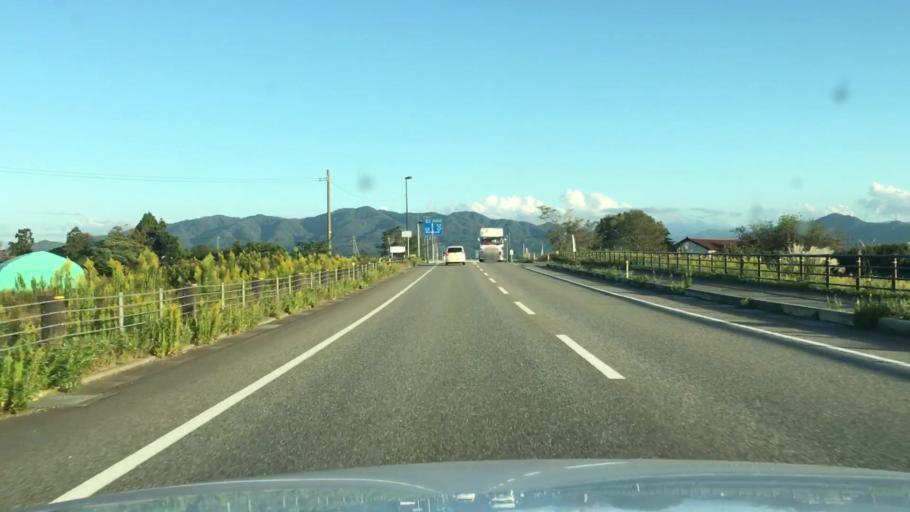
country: JP
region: Niigata
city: Murakami
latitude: 38.1223
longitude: 139.4066
